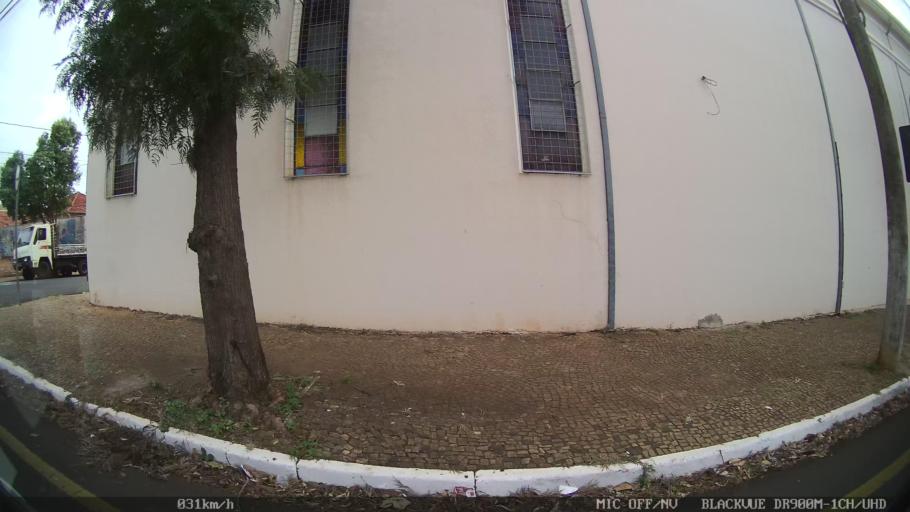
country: BR
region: Sao Paulo
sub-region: Sao Jose Do Rio Preto
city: Sao Jose do Rio Preto
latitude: -20.8152
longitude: -49.3705
